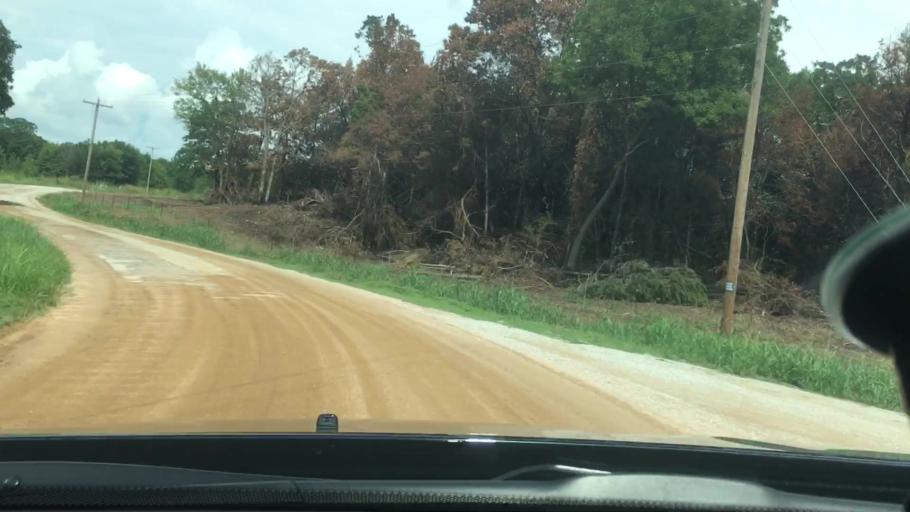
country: US
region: Oklahoma
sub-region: Carter County
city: Dickson
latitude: 34.2406
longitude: -96.9157
